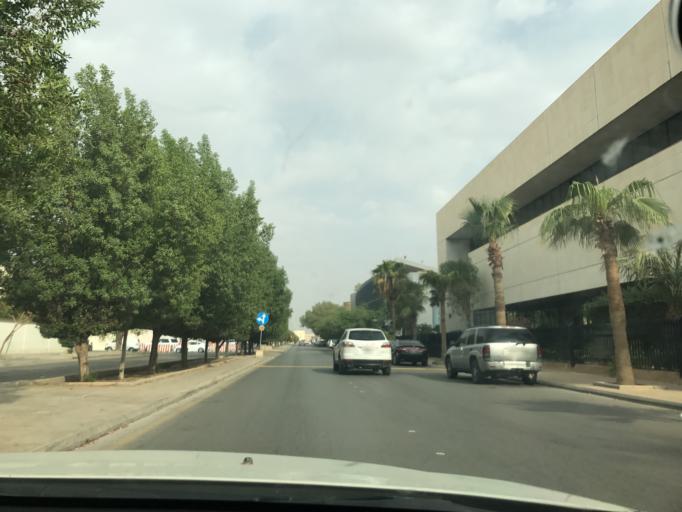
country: SA
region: Ar Riyad
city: Riyadh
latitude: 24.7064
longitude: 46.7097
